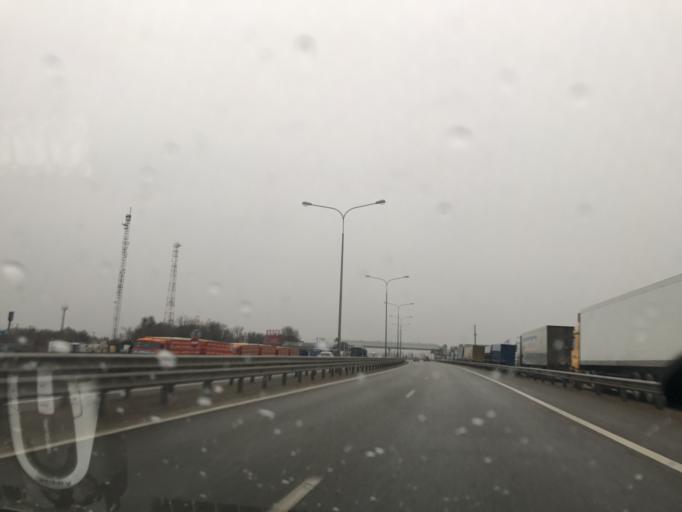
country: RU
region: Krasnodarskiy
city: Krylovskaya
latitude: 46.2826
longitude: 39.8299
